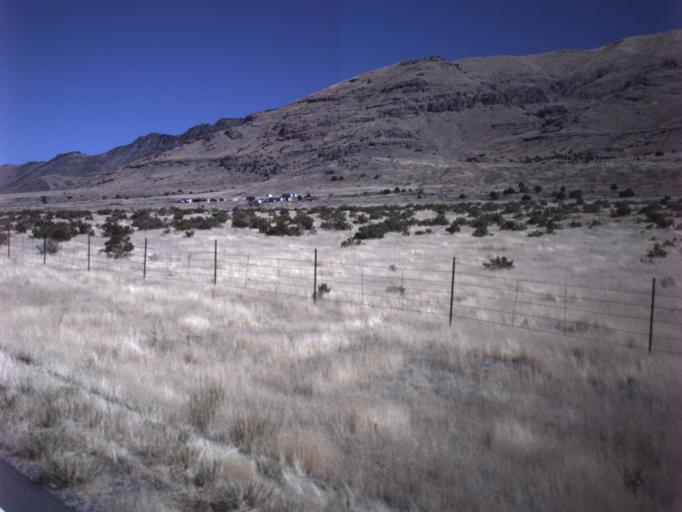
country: US
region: Utah
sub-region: Tooele County
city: Grantsville
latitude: 40.6732
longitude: -112.6732
